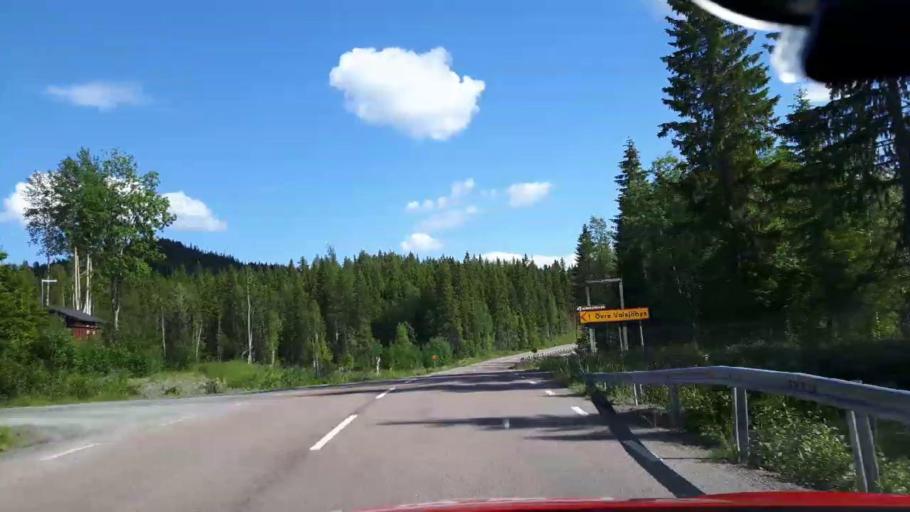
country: SE
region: Jaemtland
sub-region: Krokoms Kommun
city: Valla
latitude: 64.0647
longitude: 14.1481
